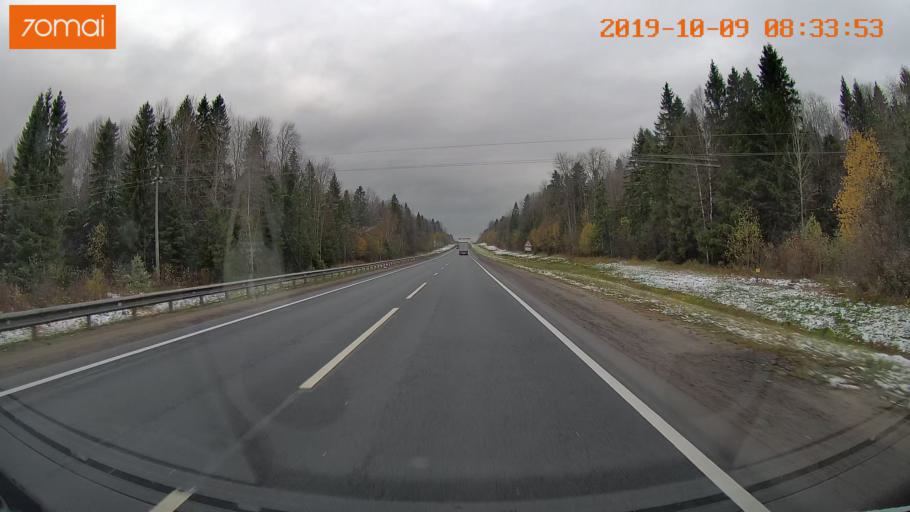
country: RU
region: Vologda
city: Gryazovets
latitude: 58.8887
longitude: 40.1893
